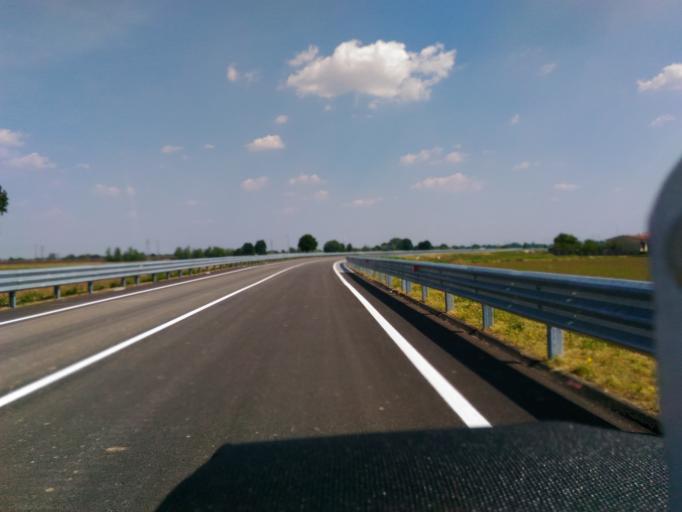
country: IT
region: Lombardy
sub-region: Citta metropolitana di Milano
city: Dresano
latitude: 45.3764
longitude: 9.3625
